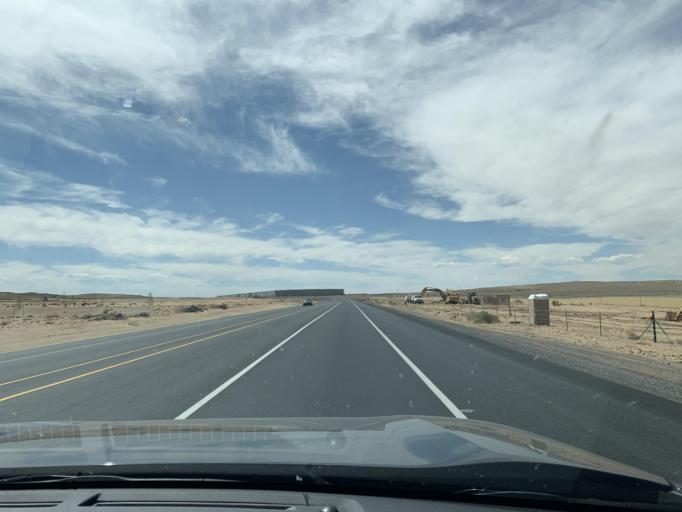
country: US
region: New Mexico
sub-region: Valencia County
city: Los Lunas
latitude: 34.8221
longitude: -106.7987
